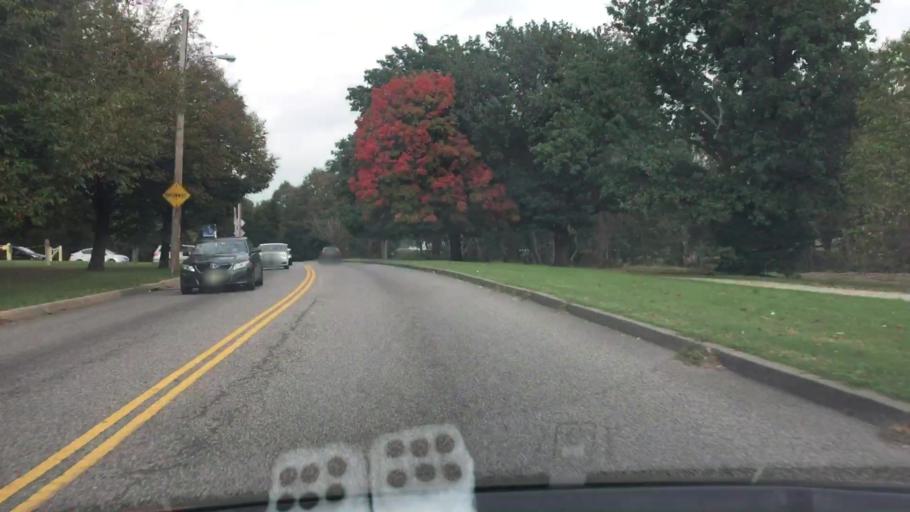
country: US
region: Pennsylvania
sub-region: Montgomery County
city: Bala-Cynwyd
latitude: 39.9854
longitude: -75.2115
